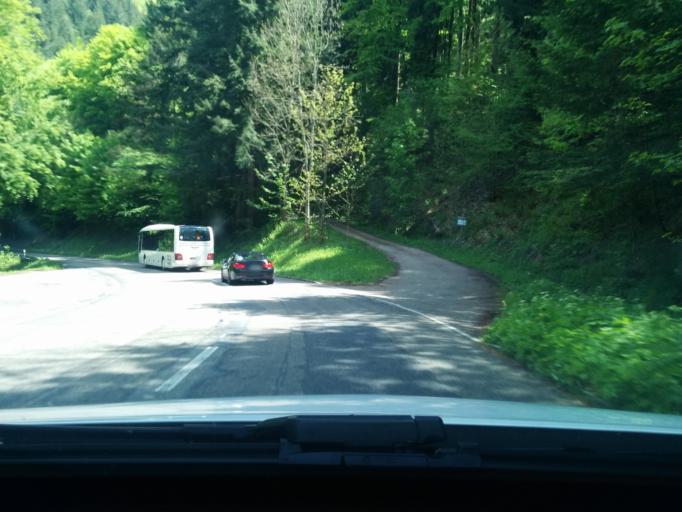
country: DE
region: Baden-Wuerttemberg
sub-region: Freiburg Region
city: Horben
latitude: 47.9249
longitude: 7.8775
